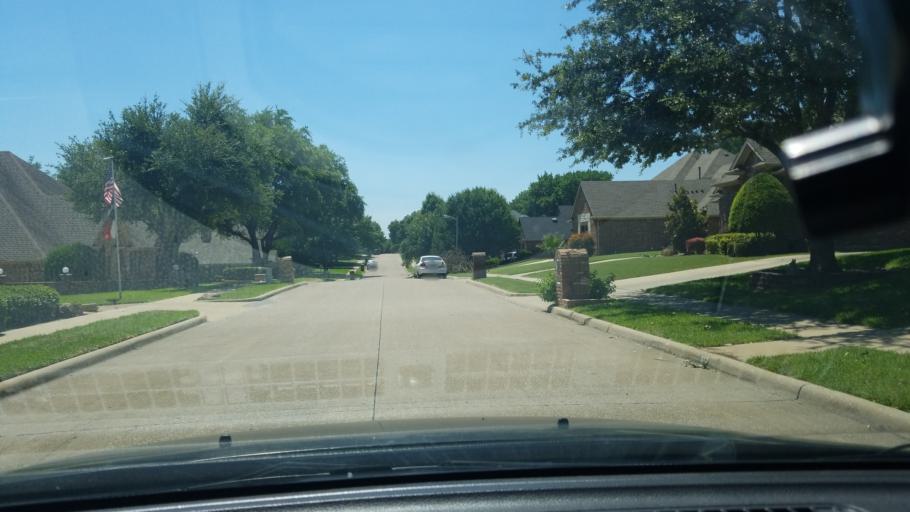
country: US
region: Texas
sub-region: Dallas County
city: Mesquite
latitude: 32.7598
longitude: -96.6060
